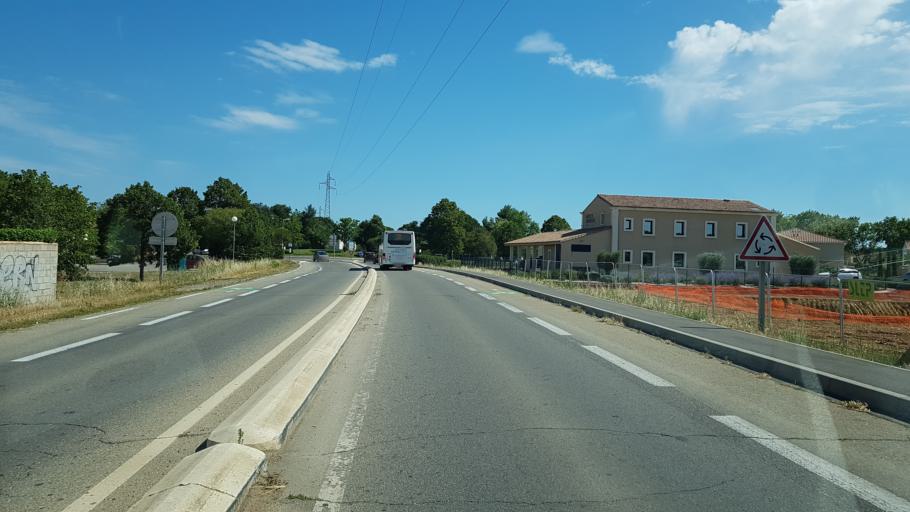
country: FR
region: Provence-Alpes-Cote d'Azur
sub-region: Departement des Bouches-du-Rhone
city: Saint-Martin-de-Crau
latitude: 43.6388
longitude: 4.7983
